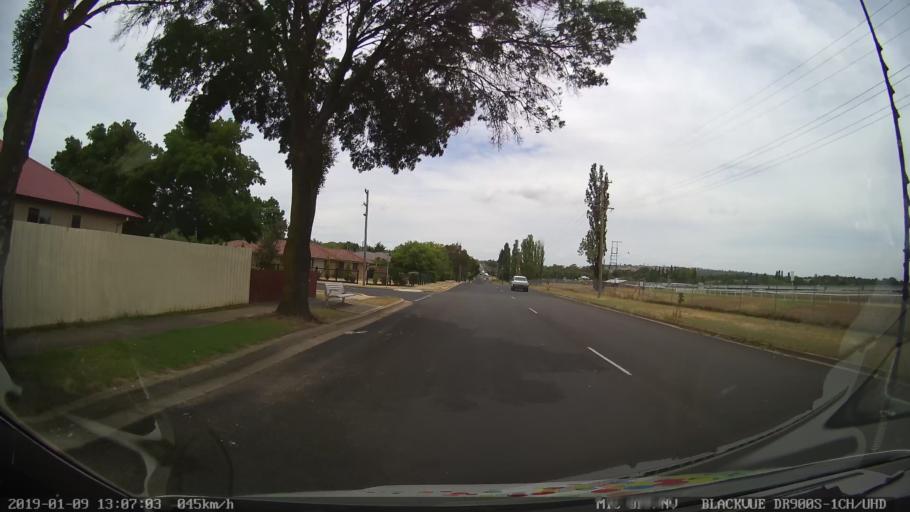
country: AU
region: New South Wales
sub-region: Armidale Dumaresq
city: Armidale
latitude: -30.5169
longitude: 151.6806
